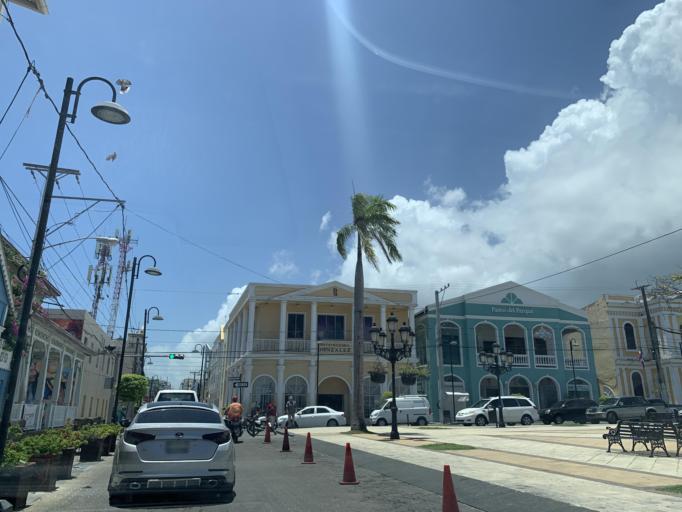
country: DO
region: Puerto Plata
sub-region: Puerto Plata
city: Puerto Plata
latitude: 19.7980
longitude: -70.6931
